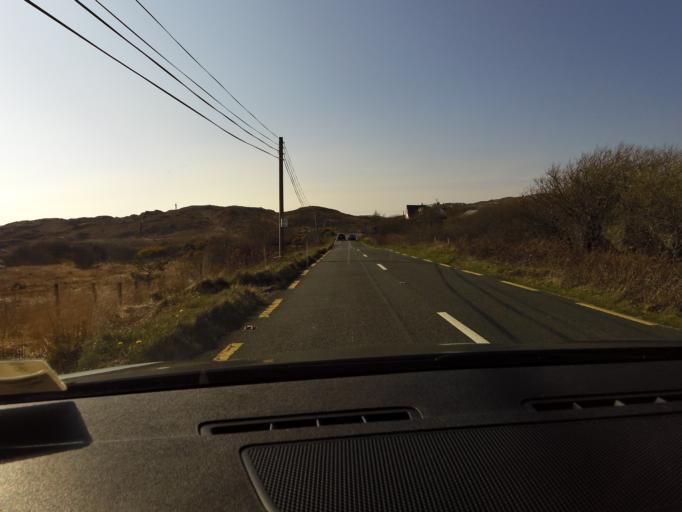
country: IE
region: Connaught
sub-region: County Galway
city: Clifden
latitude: 53.4832
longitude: -9.9742
